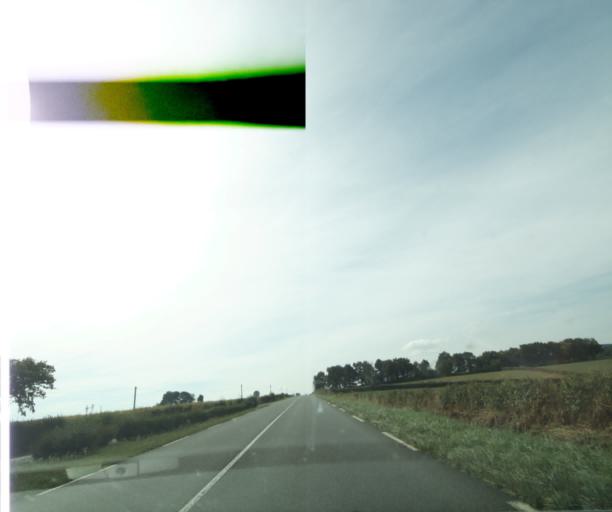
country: FR
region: Auvergne
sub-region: Departement de l'Allier
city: Le Donjon
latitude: 46.3391
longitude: 3.7743
